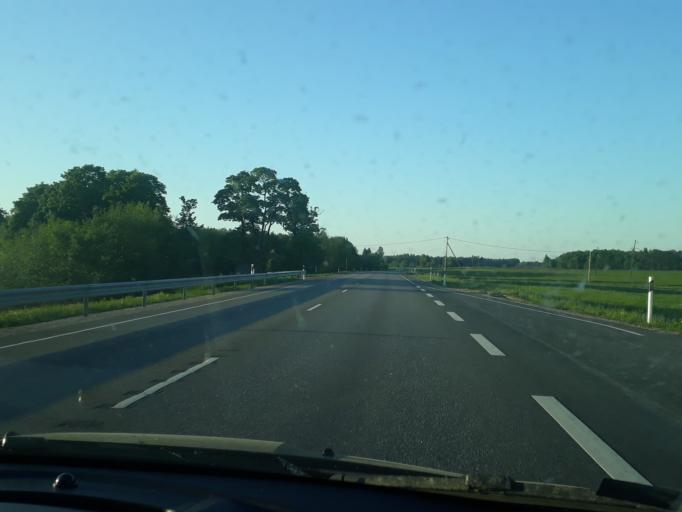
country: EE
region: Paernumaa
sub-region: Tootsi vald
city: Tootsi
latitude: 58.5657
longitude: 24.8724
